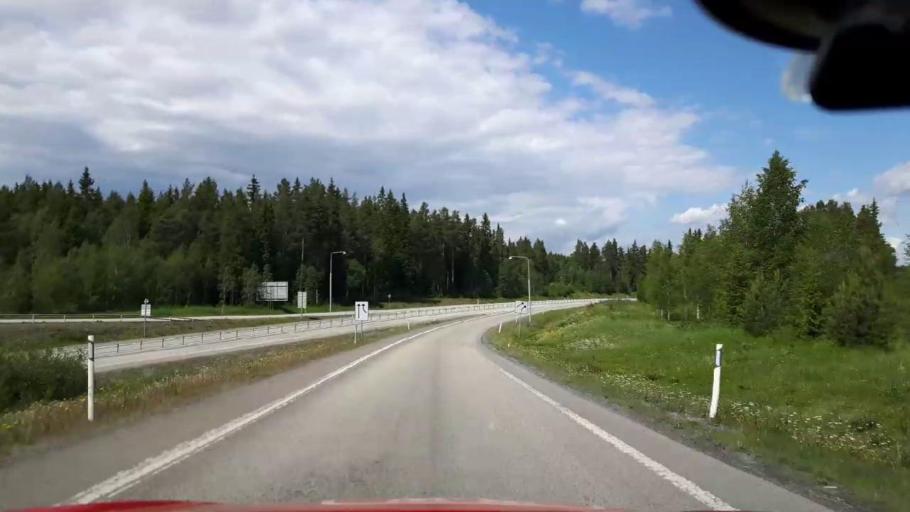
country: SE
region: Jaemtland
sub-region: OEstersunds Kommun
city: Ostersund
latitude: 63.1808
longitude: 14.6906
